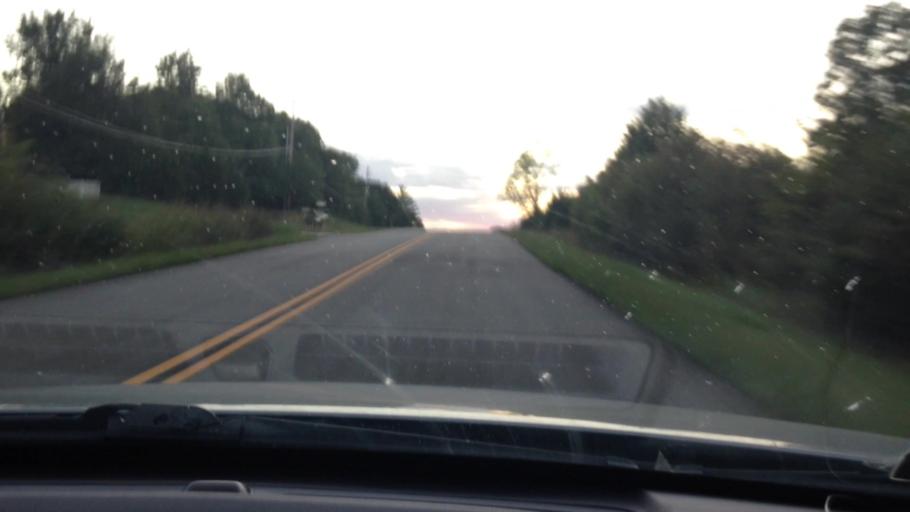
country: US
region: Kansas
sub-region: Leavenworth County
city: Lansing
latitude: 39.1869
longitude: -94.8797
